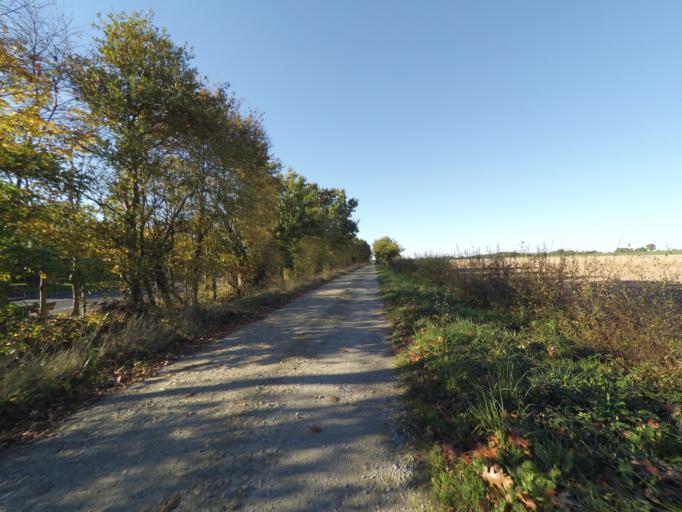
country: FR
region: Pays de la Loire
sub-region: Departement de la Loire-Atlantique
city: La Planche
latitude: 47.0199
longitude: -1.3940
